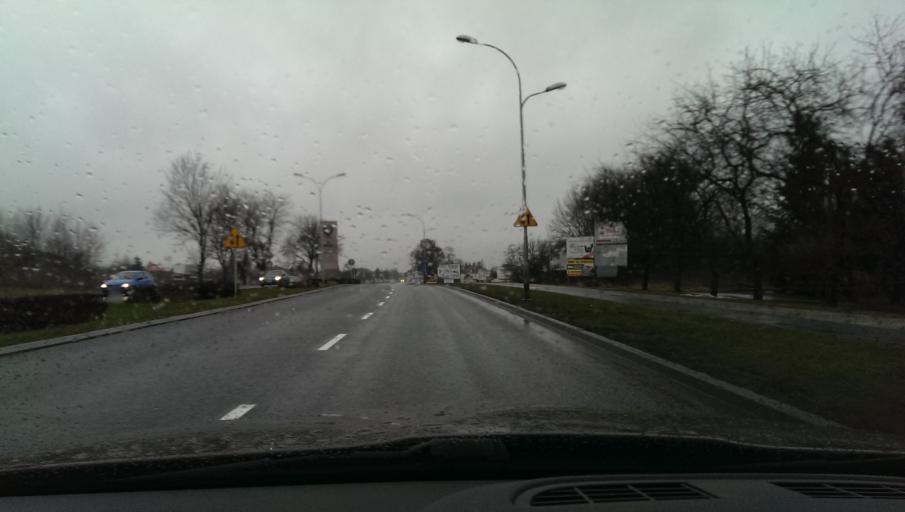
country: PL
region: Subcarpathian Voivodeship
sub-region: Rzeszow
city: Rzeszow
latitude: 50.0721
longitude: 21.9891
